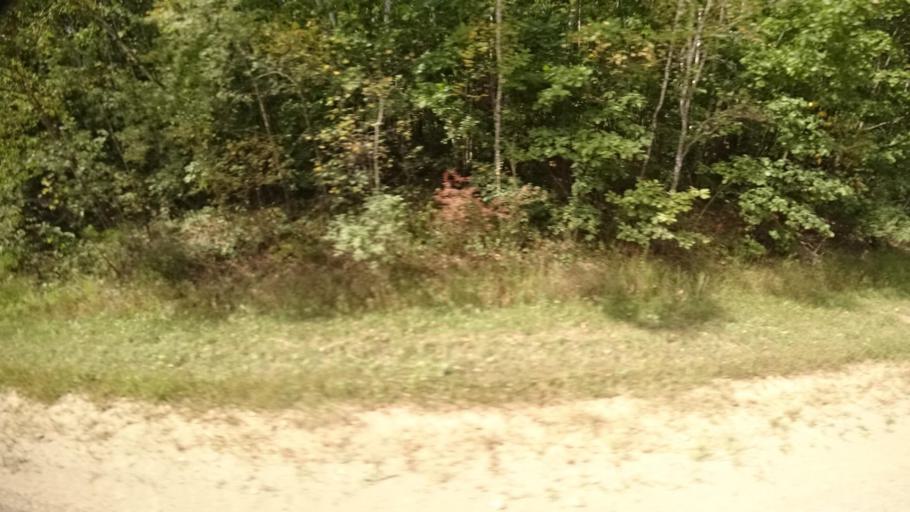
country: RU
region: Primorskiy
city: Yakovlevka
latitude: 44.6696
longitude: 133.6110
